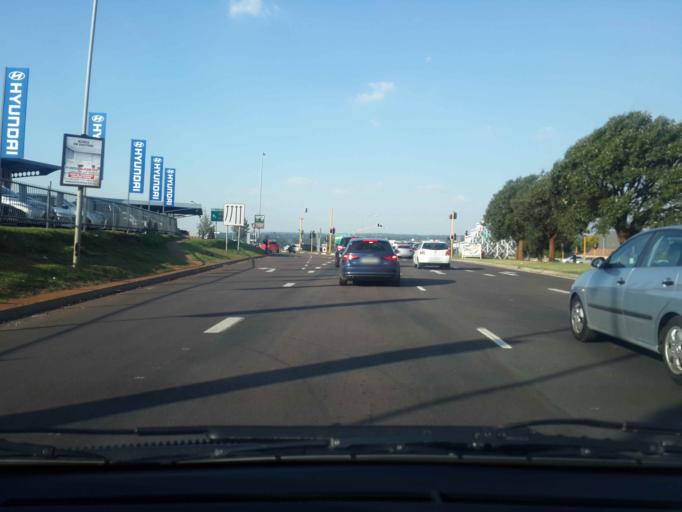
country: ZA
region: Gauteng
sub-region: City of Tshwane Metropolitan Municipality
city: Centurion
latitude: -25.8728
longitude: 28.1948
